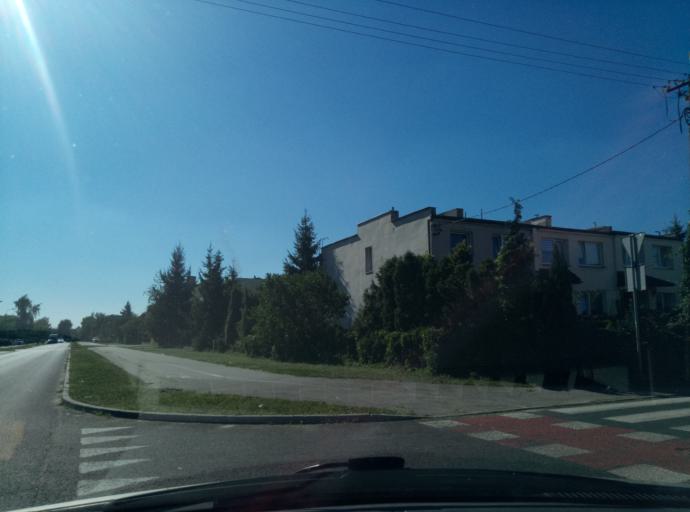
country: PL
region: Kujawsko-Pomorskie
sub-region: Torun
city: Torun
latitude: 53.0458
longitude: 18.5854
